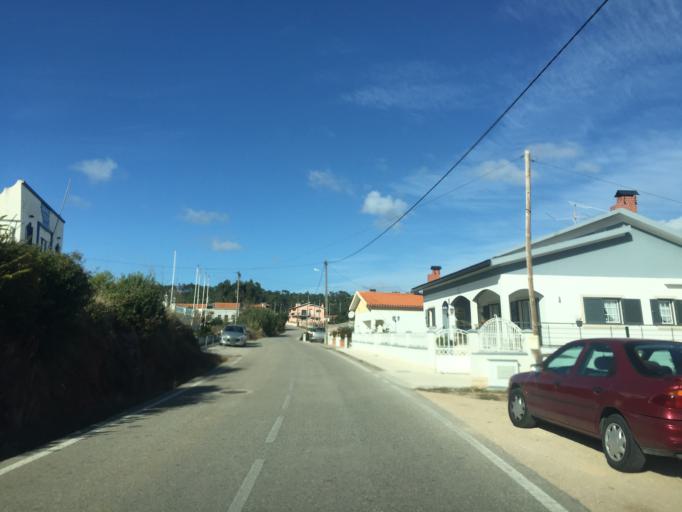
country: PT
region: Coimbra
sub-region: Figueira da Foz
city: Tavarede
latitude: 40.1802
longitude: -8.8376
